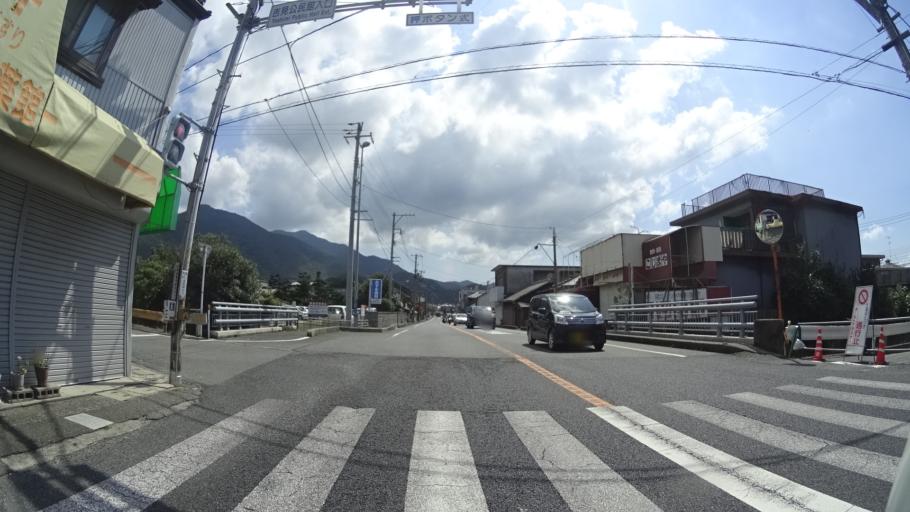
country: JP
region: Yamaguchi
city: Shimonoseki
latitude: 34.0707
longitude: 130.9012
